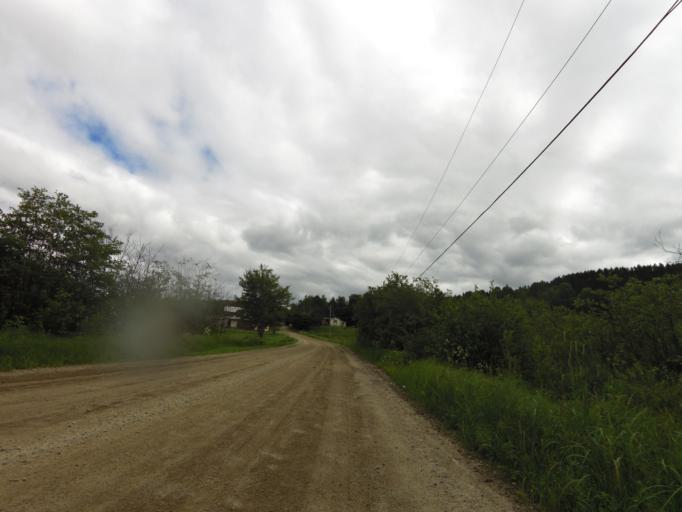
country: CA
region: Quebec
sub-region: Laurentides
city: Mont-Tremblant
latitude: 45.9387
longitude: -74.6508
